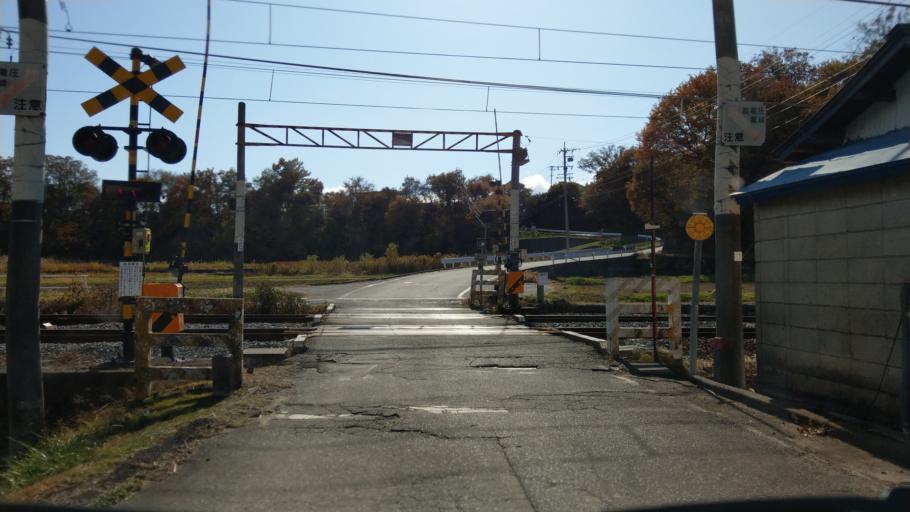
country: JP
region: Nagano
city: Komoro
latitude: 36.3103
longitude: 138.4699
